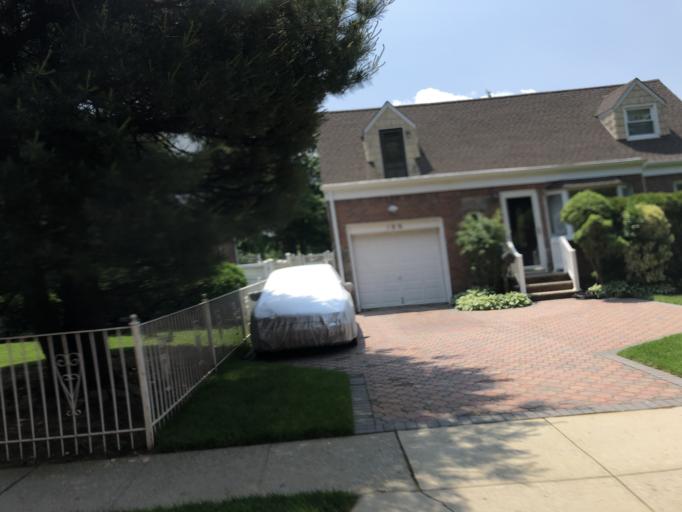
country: US
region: New York
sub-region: Nassau County
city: Elmont
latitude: 40.6871
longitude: -73.7199
